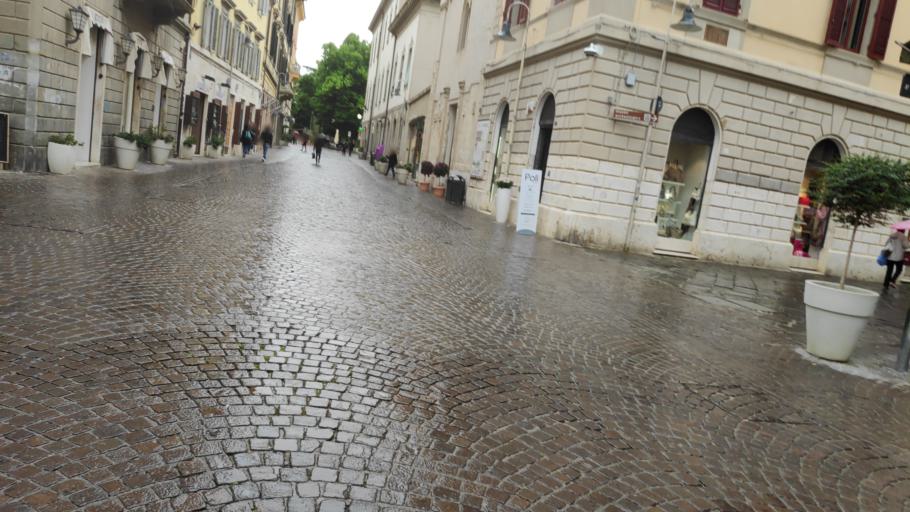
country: IT
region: Tuscany
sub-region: Provincia di Grosseto
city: Grosseto
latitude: 42.7615
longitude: 11.1130
